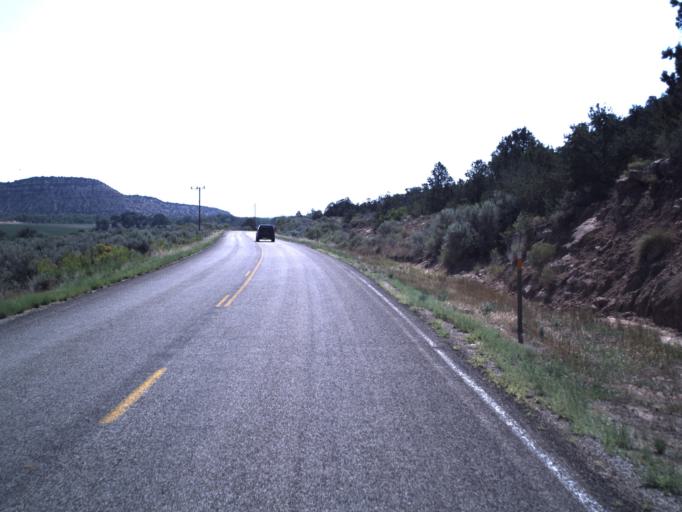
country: US
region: Utah
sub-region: Duchesne County
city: Duchesne
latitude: 40.2954
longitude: -110.5124
